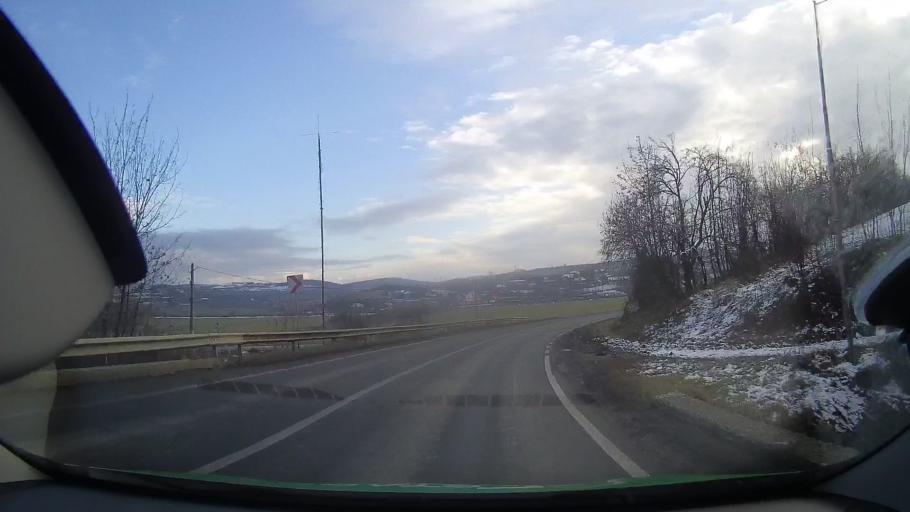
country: RO
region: Mures
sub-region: Comuna Cucerdea
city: Cucerdea
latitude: 46.4096
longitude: 24.2679
